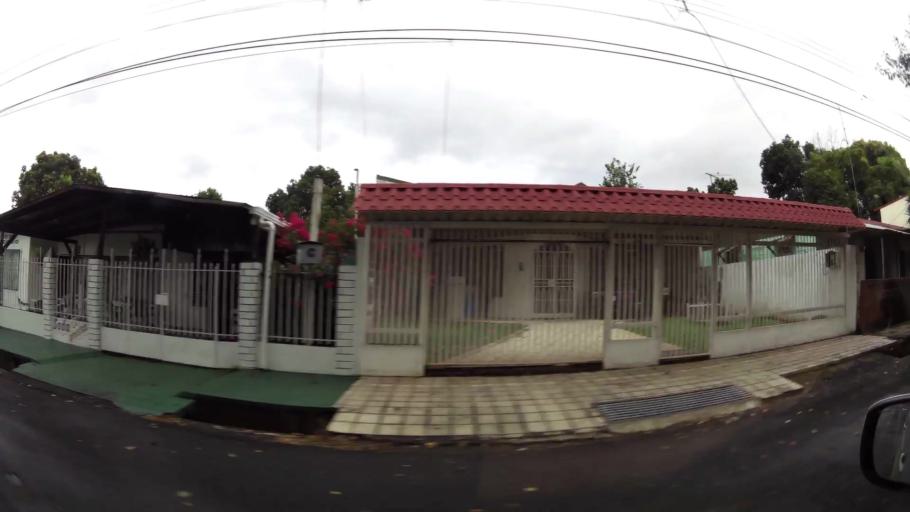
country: CR
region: Puntarenas
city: Esparza
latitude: 9.9934
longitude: -84.6665
